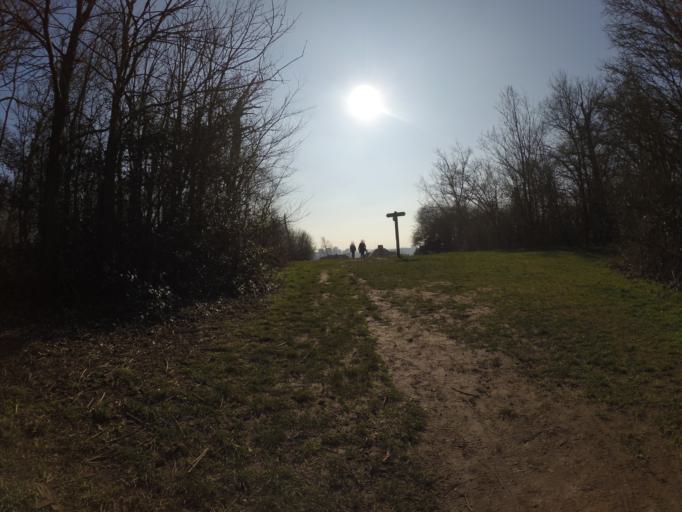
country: GB
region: England
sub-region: Greater London
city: Wembley
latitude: 51.5727
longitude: -0.2797
